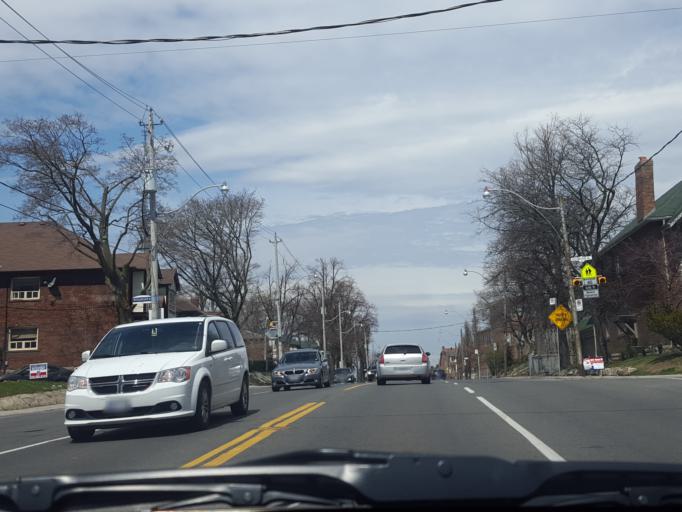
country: CA
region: Ontario
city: Toronto
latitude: 43.7059
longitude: -79.4096
